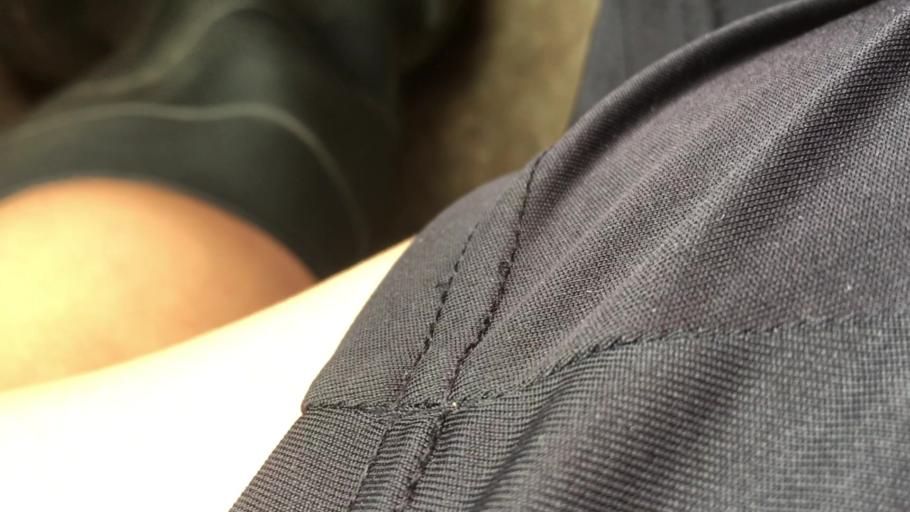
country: US
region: Maryland
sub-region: Worcester County
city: Pocomoke City
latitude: 38.0659
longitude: -75.5262
